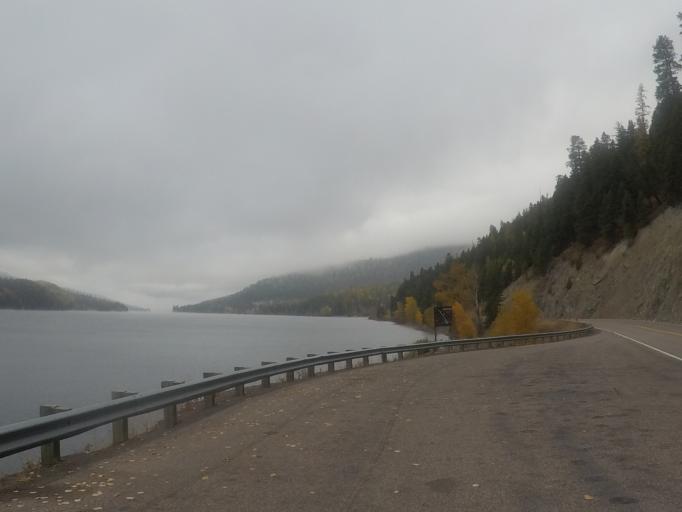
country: US
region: Montana
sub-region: Flathead County
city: Bigfork
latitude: 47.9406
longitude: -113.8709
